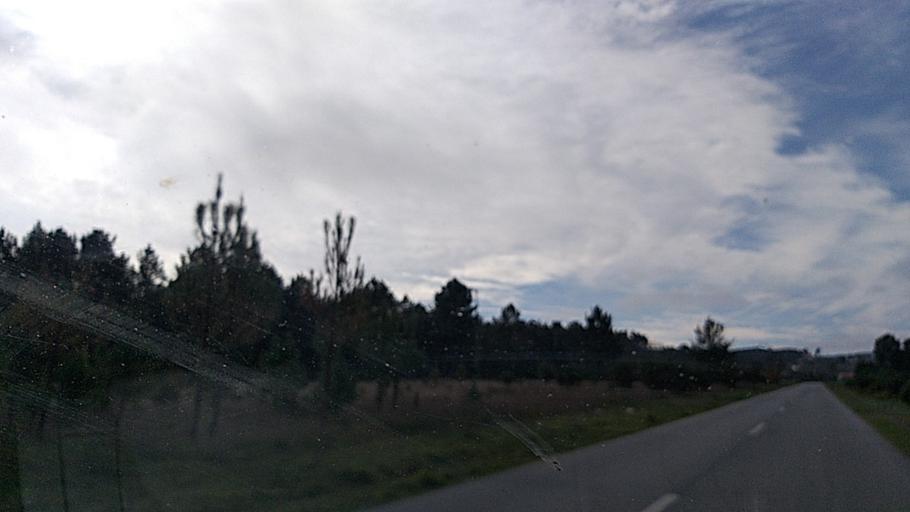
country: PT
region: Guarda
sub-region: Fornos de Algodres
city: Fornos de Algodres
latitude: 40.6653
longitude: -7.5301
